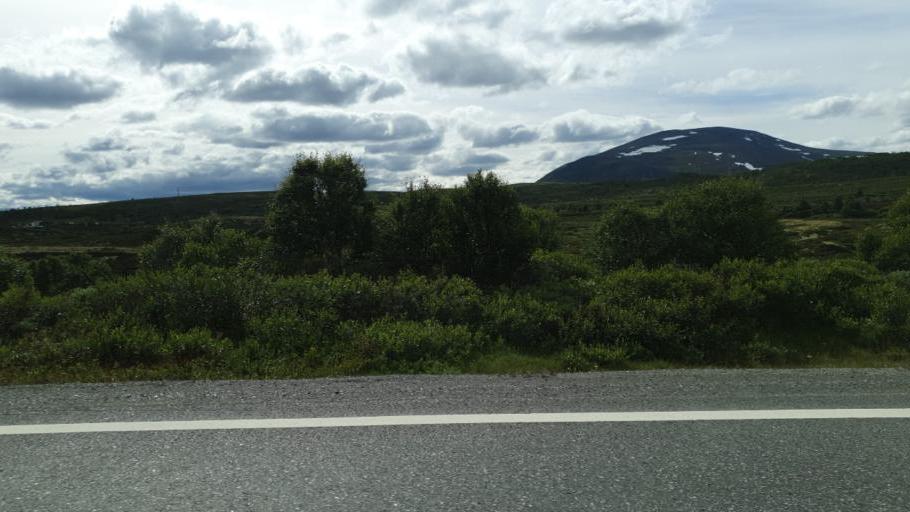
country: NO
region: Sor-Trondelag
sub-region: Oppdal
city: Oppdal
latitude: 62.2820
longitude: 9.5996
